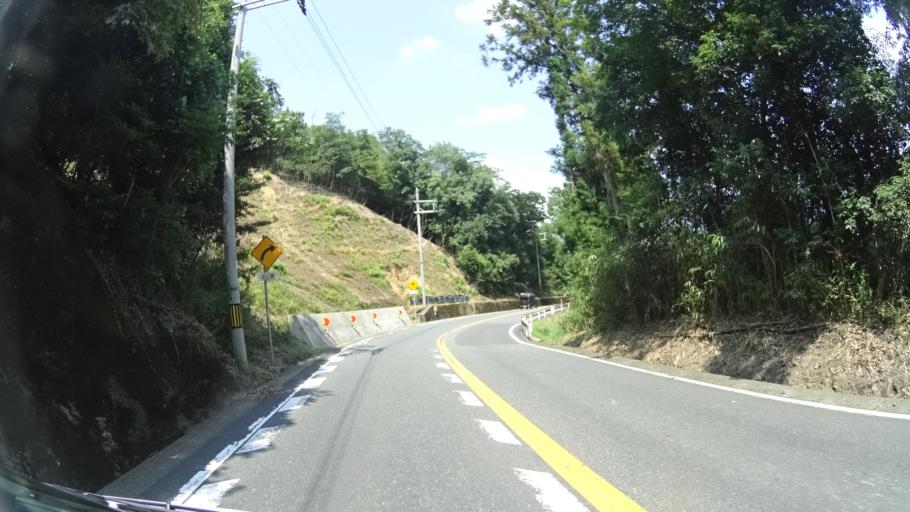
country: JP
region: Kyoto
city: Fukuchiyama
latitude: 35.2657
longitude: 135.1442
